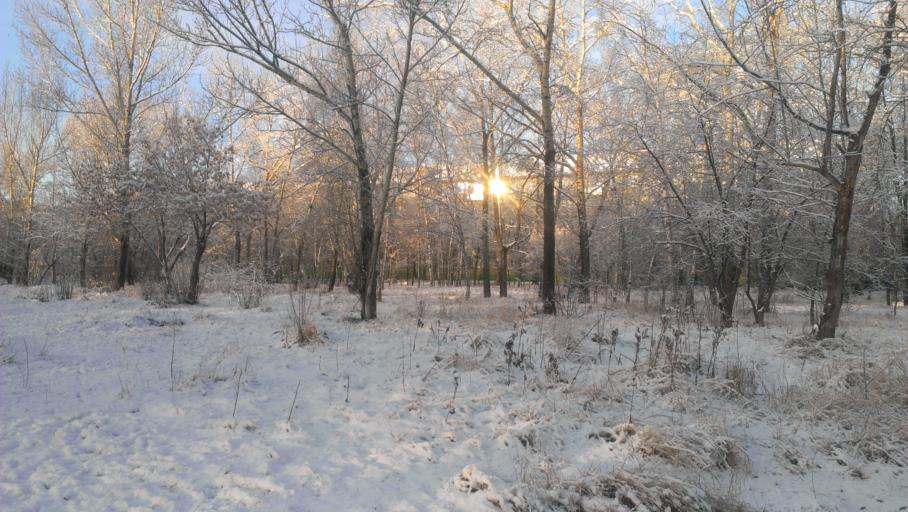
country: RU
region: Altai Krai
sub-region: Gorod Barnaulskiy
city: Barnaul
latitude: 53.3638
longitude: 83.6891
